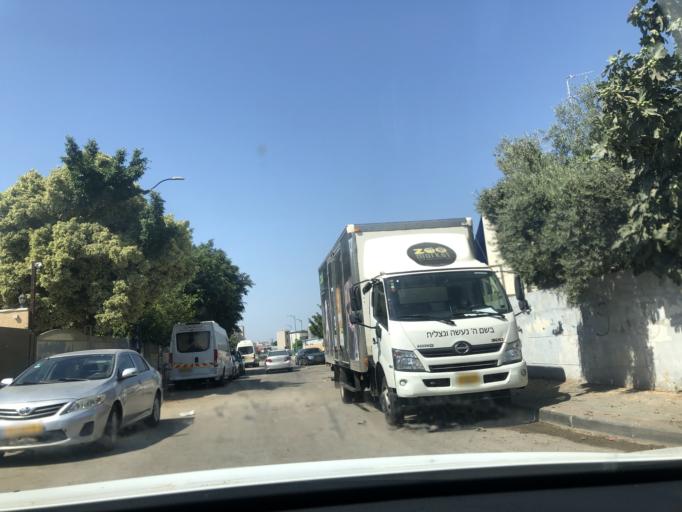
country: IL
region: Central District
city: Lod
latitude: 31.9524
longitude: 34.8740
